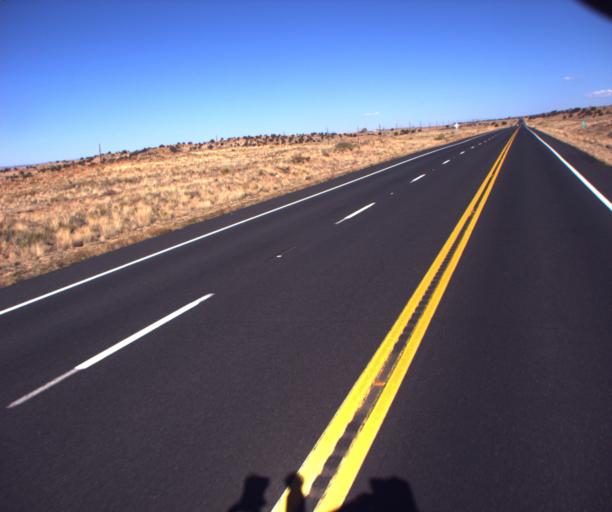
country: US
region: Arizona
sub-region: Coconino County
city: Kaibito
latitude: 36.4329
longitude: -110.7690
